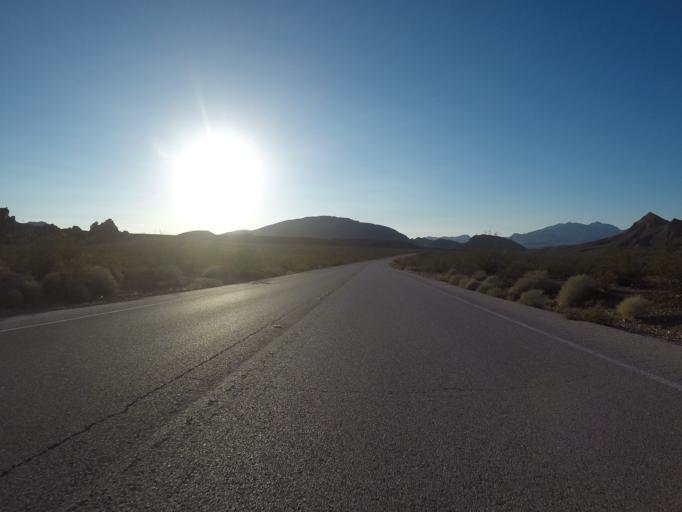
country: US
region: Nevada
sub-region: Clark County
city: Moapa Valley
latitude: 36.2418
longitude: -114.5236
